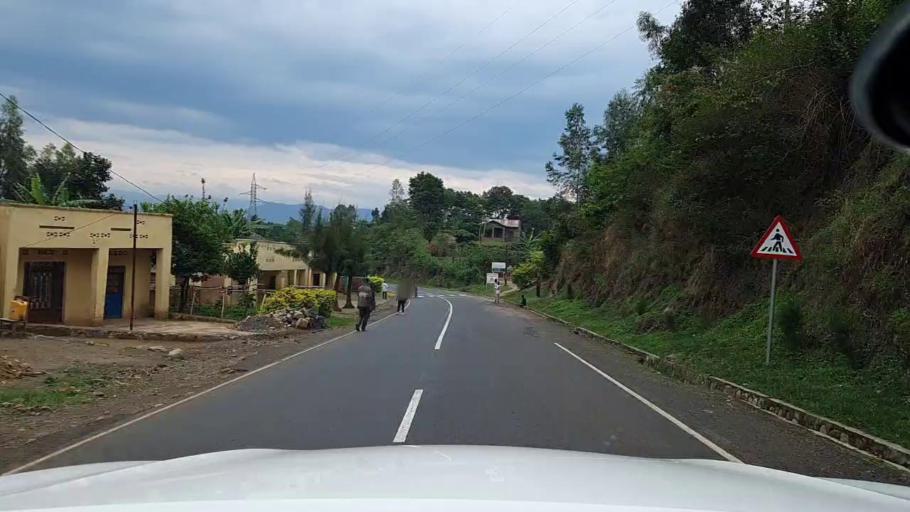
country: RW
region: Western Province
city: Cyangugu
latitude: -2.6585
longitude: 28.9763
